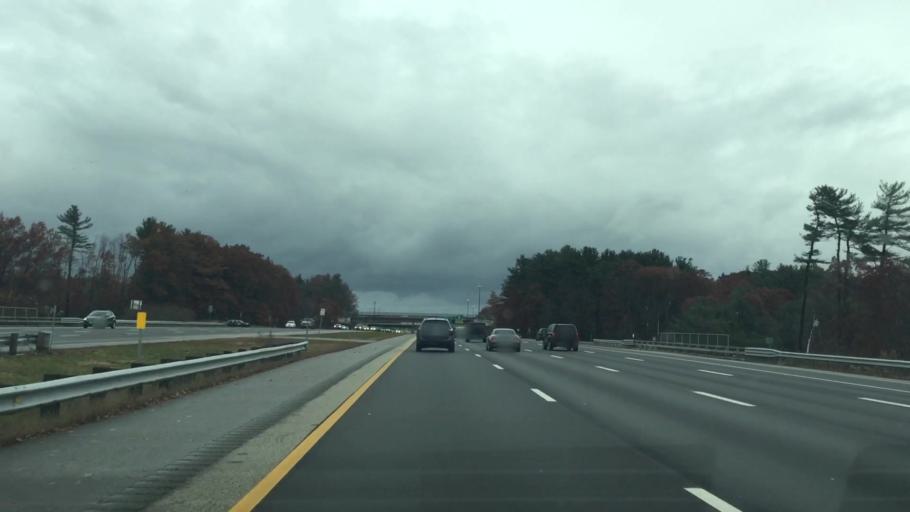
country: US
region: New Hampshire
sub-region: Rockingham County
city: Hampton
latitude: 42.9517
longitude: -70.8584
